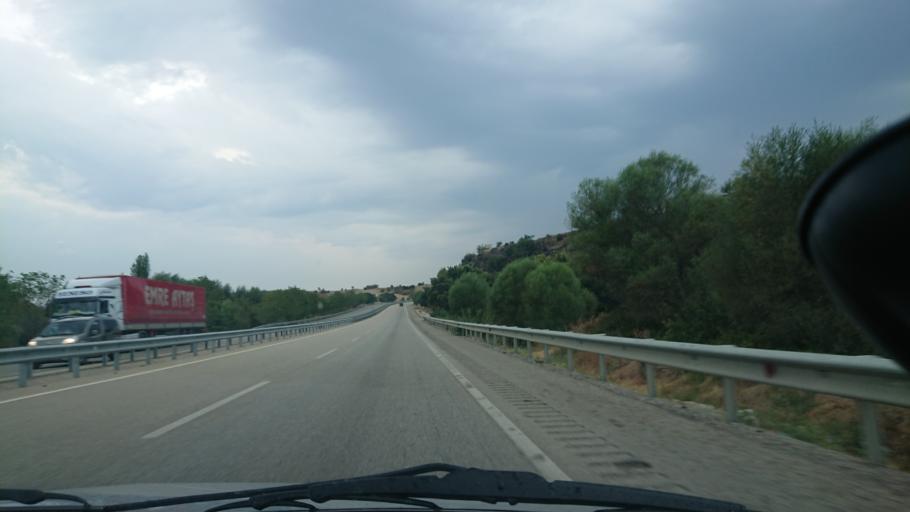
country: TR
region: Manisa
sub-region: Kula
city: Kula
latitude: 38.5885
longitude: 28.7795
